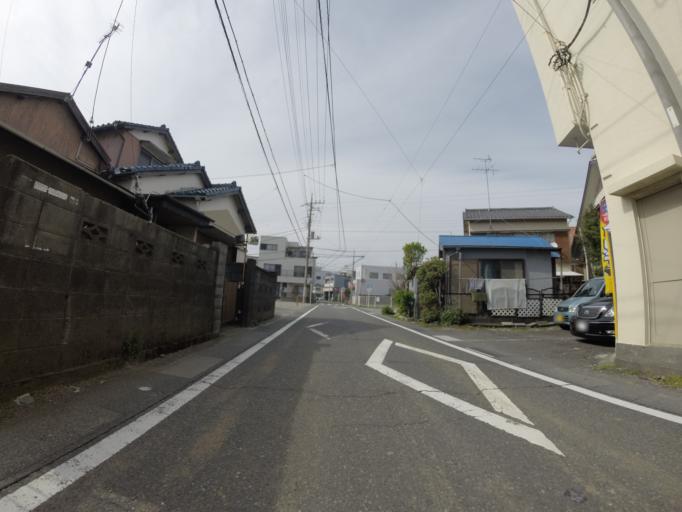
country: JP
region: Shizuoka
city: Numazu
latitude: 35.0838
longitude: 138.8707
